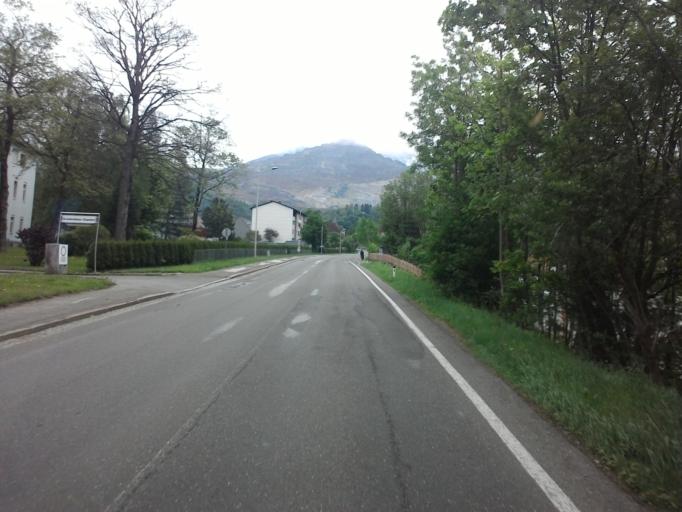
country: AT
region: Styria
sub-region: Politischer Bezirk Leoben
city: Eisenerz
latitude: 47.5471
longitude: 14.8808
